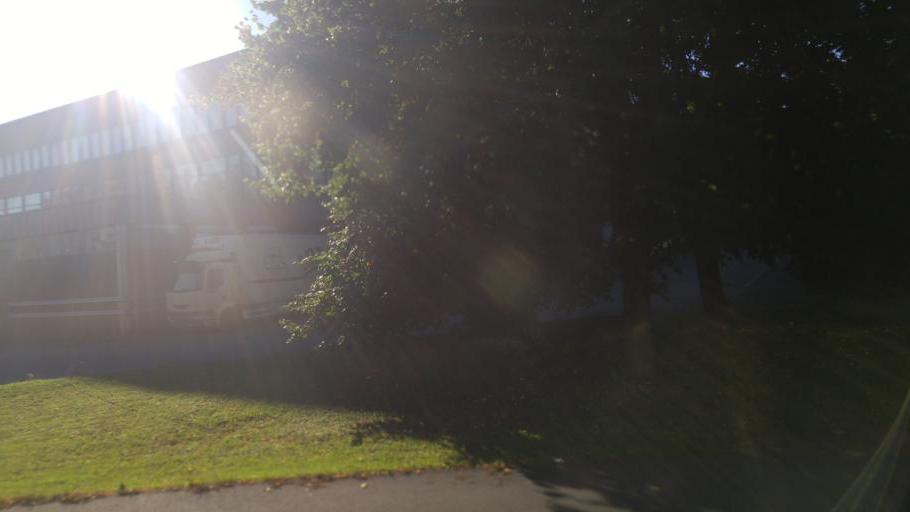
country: NO
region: Akershus
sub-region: Asker
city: Billingstad
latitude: 59.8737
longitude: 10.4886
